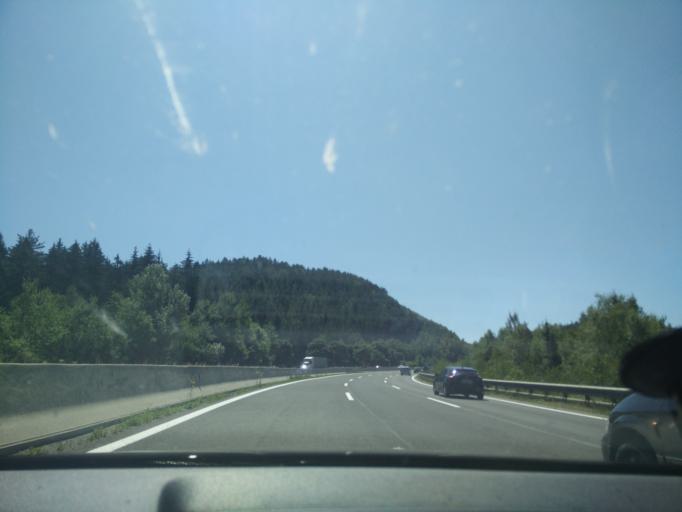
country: AT
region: Lower Austria
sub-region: Politischer Bezirk Neunkirchen
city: Edlitz
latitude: 47.5775
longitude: 16.1126
